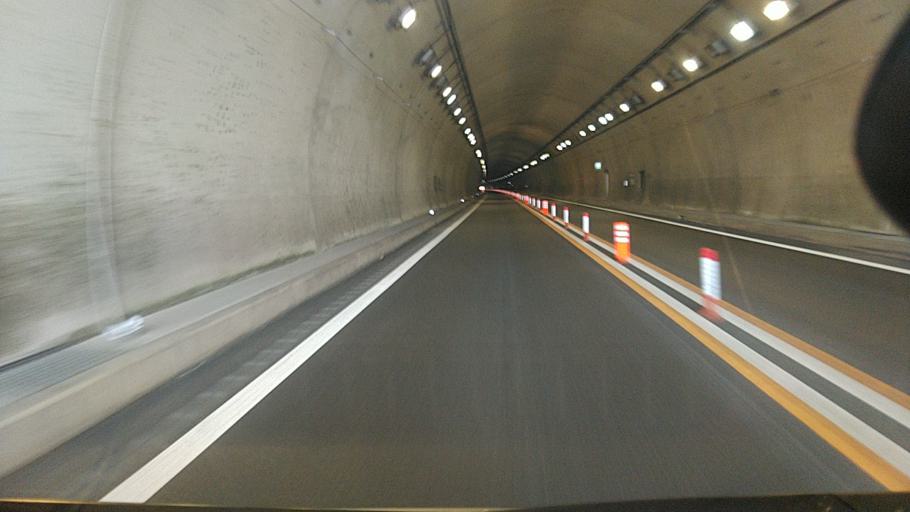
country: JP
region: Chiba
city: Kisarazu
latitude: 35.3591
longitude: 140.0654
